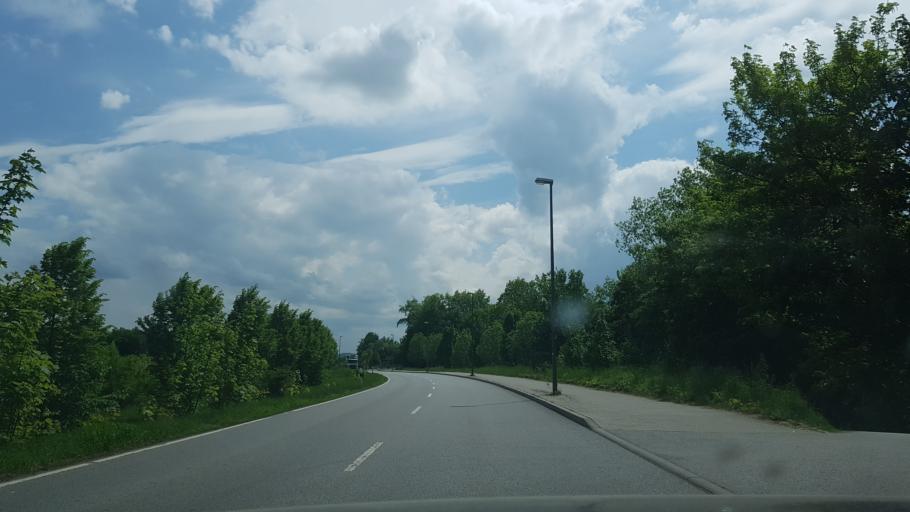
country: DE
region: Saxony
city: Freital
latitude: 51.0333
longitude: 13.6350
